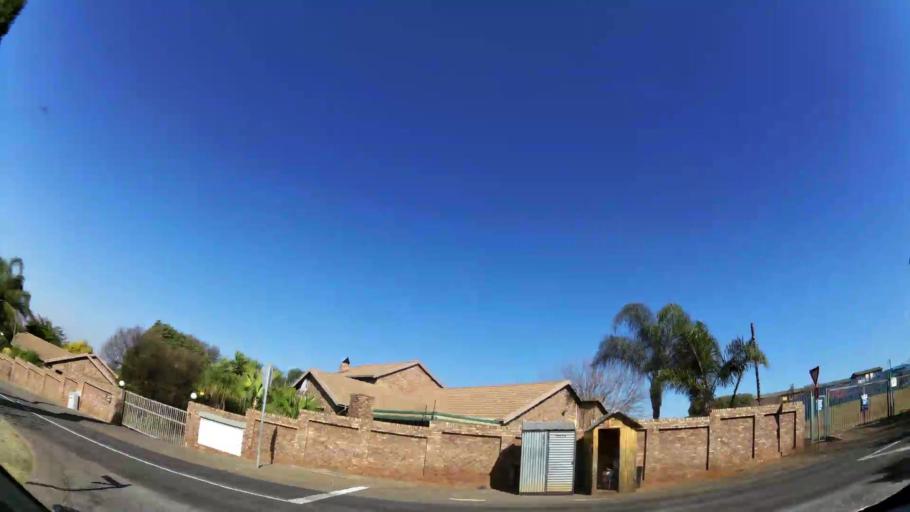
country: ZA
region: Gauteng
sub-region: City of Tshwane Metropolitan Municipality
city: Centurion
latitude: -25.8469
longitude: 28.1674
